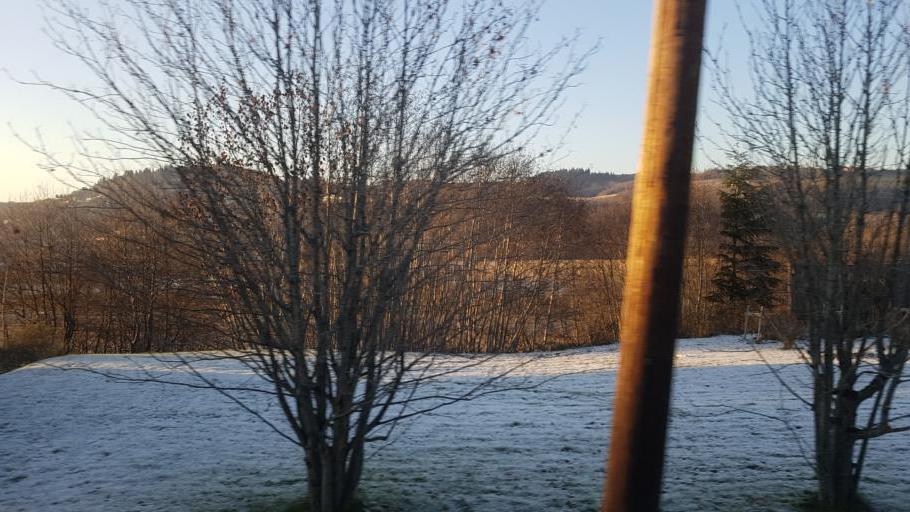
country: NO
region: Sor-Trondelag
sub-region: Melhus
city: Melhus
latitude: 63.2948
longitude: 10.2815
